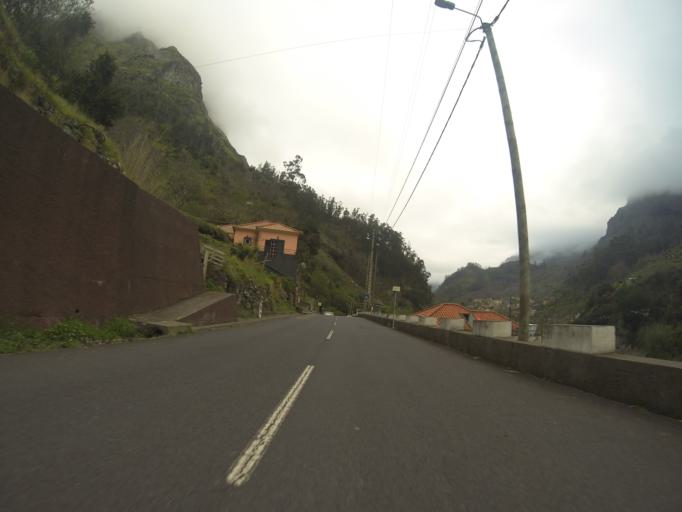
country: PT
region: Madeira
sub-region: Camara de Lobos
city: Curral das Freiras
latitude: 32.7338
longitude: -16.9683
